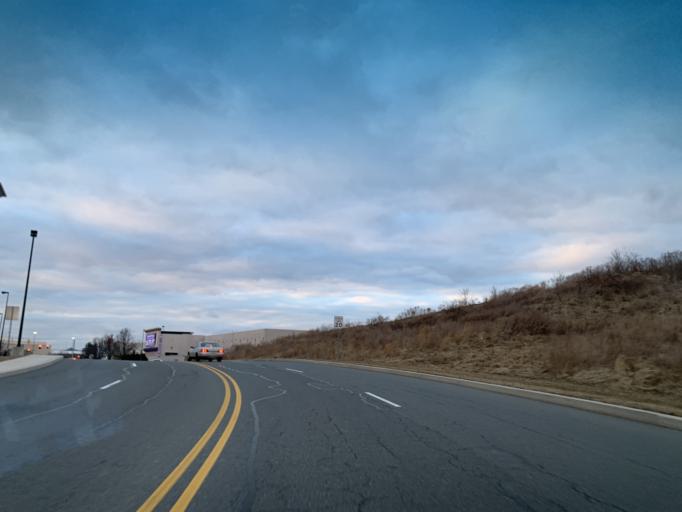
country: US
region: Delaware
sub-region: New Castle County
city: Bear
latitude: 39.6745
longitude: -75.6478
